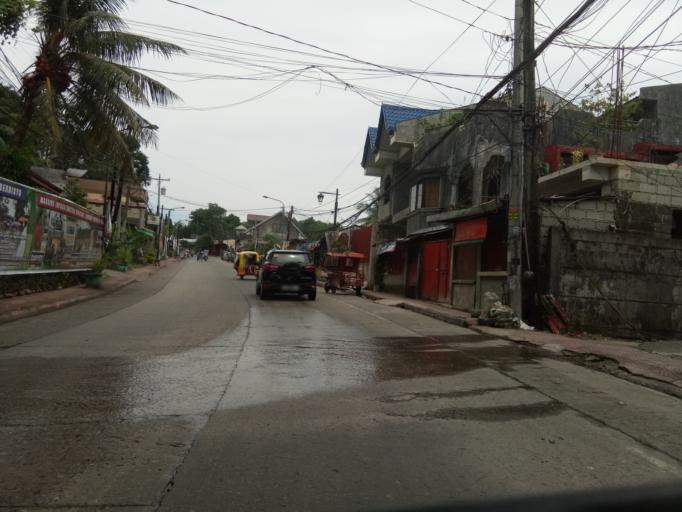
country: PH
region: Caraga
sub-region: Province of Surigao del Norte
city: Surigao
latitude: 9.7840
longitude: 125.4913
